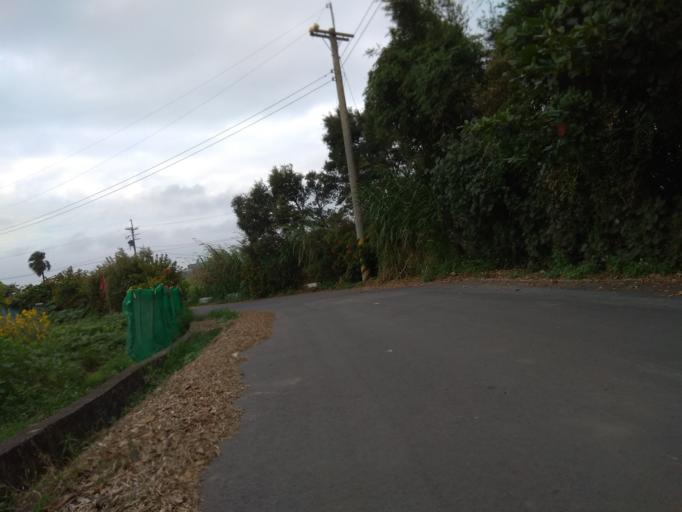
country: TW
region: Taiwan
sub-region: Hsinchu
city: Zhubei
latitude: 24.9782
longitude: 121.0356
